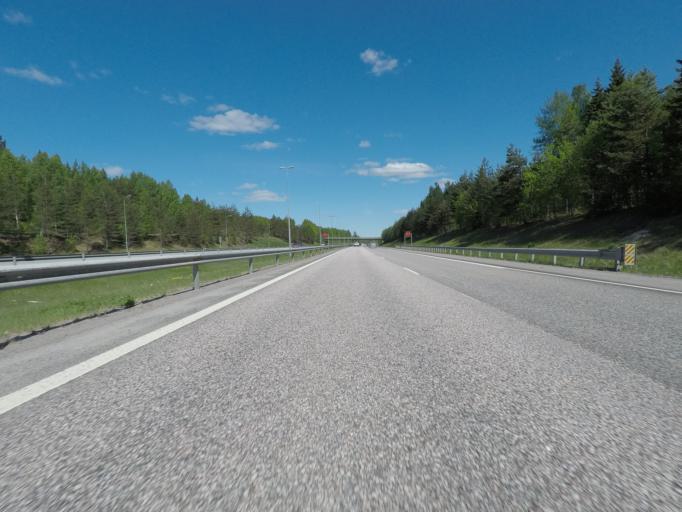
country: FI
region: Uusimaa
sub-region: Helsinki
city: Nurmijaervi
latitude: 60.3575
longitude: 24.8085
